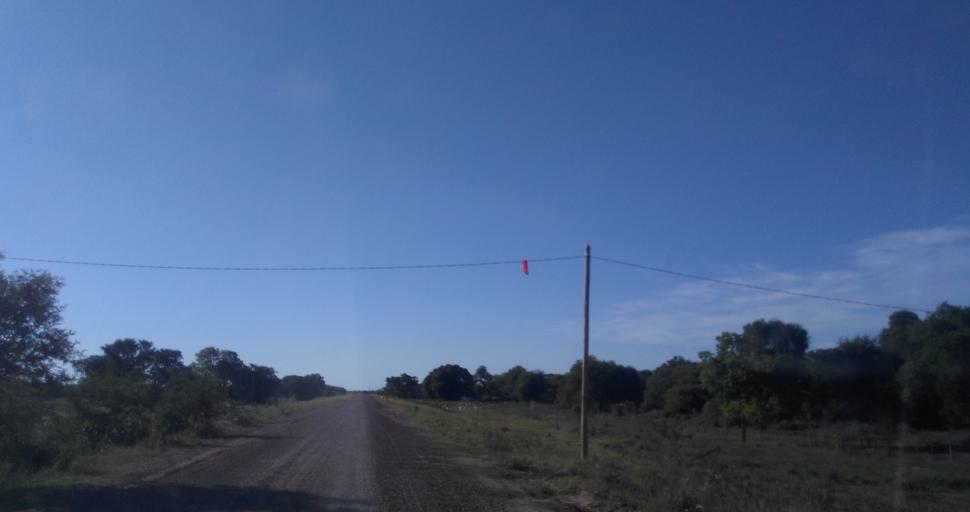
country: AR
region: Chaco
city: Resistencia
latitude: -27.4162
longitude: -58.9397
